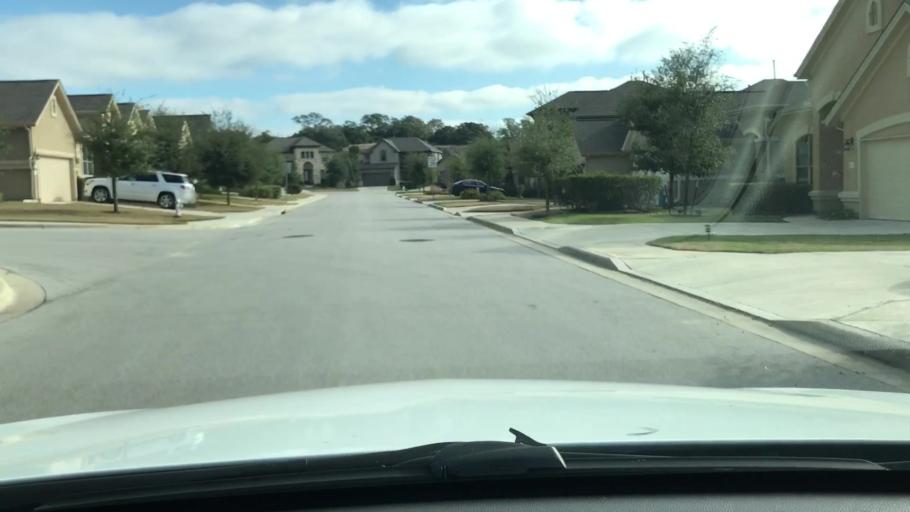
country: US
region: Texas
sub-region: Travis County
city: Bee Cave
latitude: 30.3137
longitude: -97.9597
